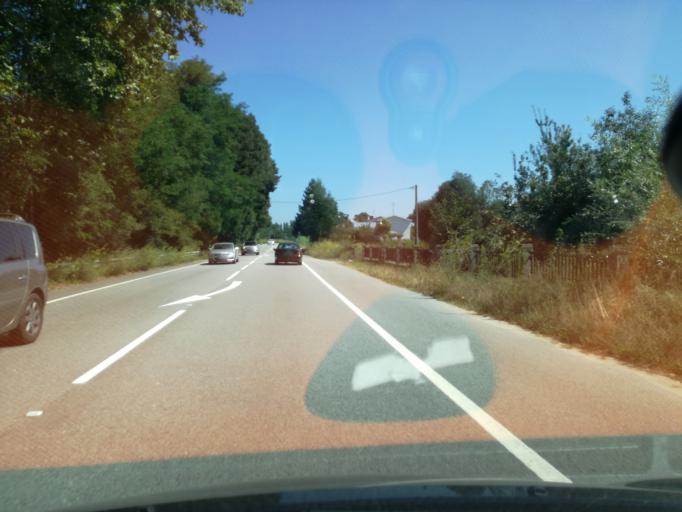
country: ES
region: Galicia
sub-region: Provincia de Pontevedra
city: O Rosal
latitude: 41.9046
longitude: -8.7988
